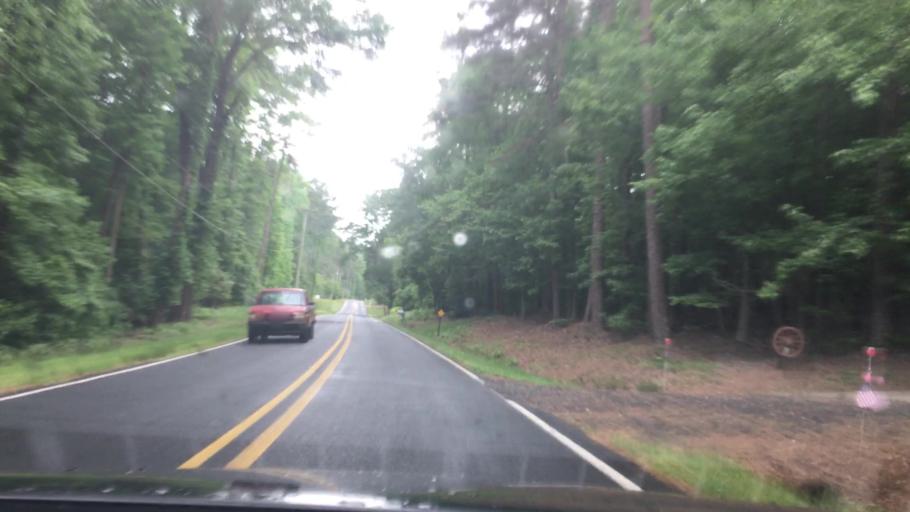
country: US
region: North Carolina
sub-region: Stanly County
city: Badin
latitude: 35.3599
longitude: -80.1170
